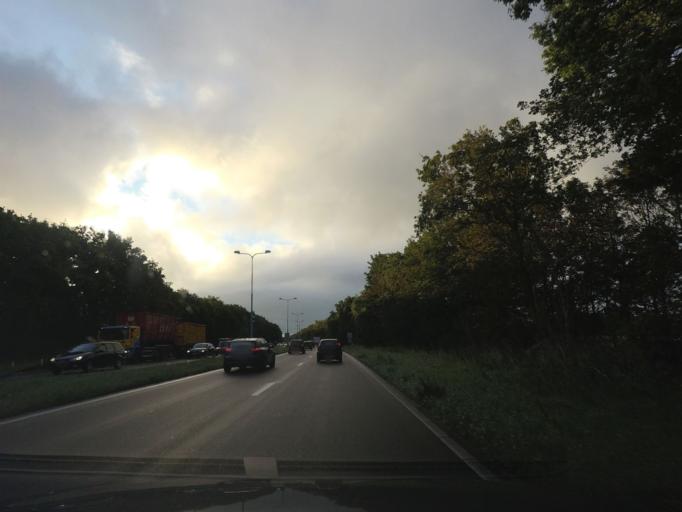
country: NL
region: North Holland
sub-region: Gemeente Alkmaar
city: Alkmaar
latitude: 52.6247
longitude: 4.7175
